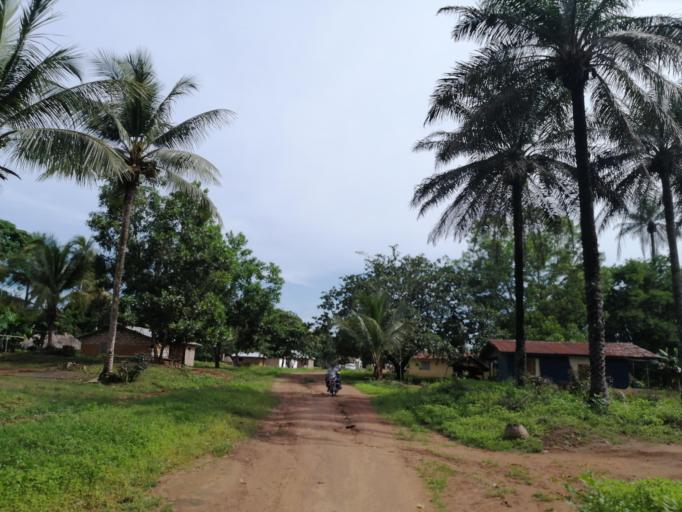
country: SL
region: Northern Province
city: Port Loko
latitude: 8.7864
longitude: -12.9247
